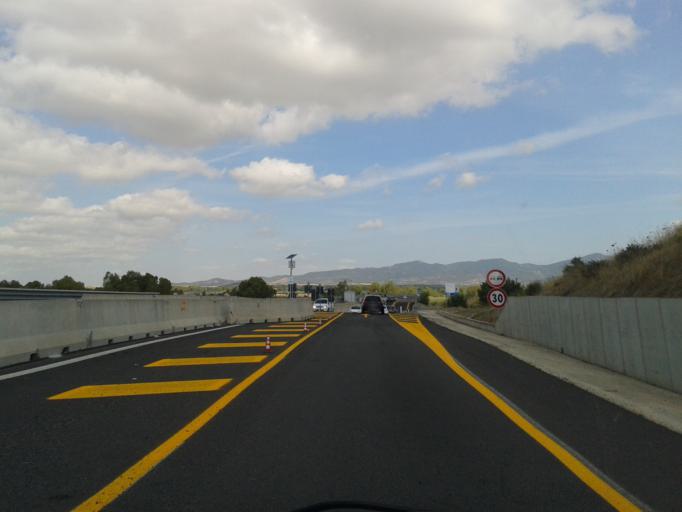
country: IT
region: Sardinia
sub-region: Provincia di Cagliari
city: Quartu Sant'Elena
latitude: 39.2432
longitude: 9.2855
